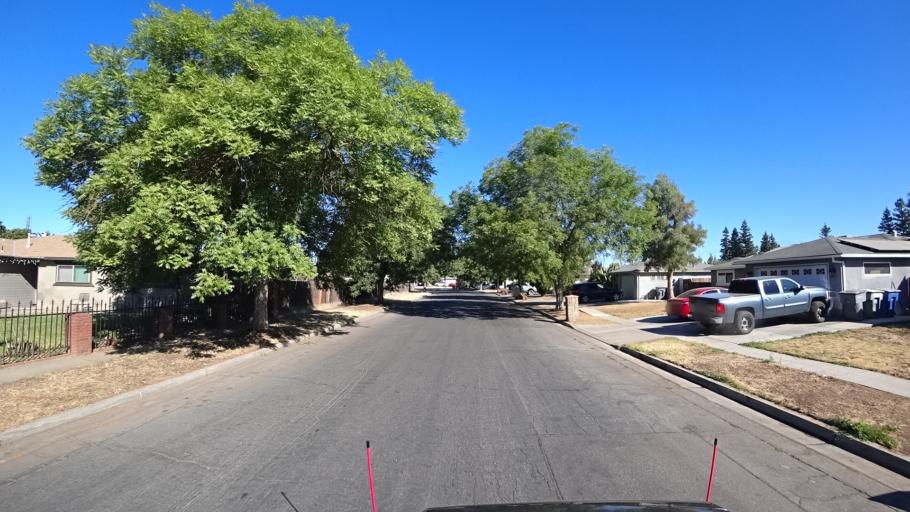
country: US
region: California
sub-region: Fresno County
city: Fresno
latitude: 36.8030
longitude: -119.8344
